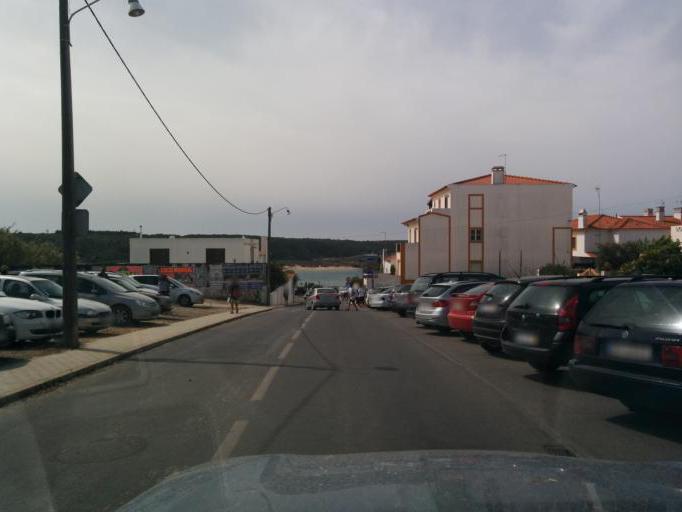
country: PT
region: Beja
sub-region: Odemira
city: Vila Nova de Milfontes
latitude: 37.7244
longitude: -8.7852
